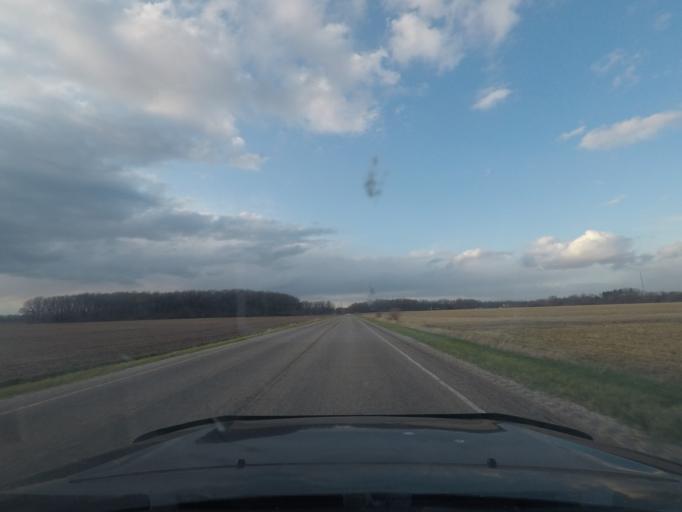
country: US
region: Indiana
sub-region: LaPorte County
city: LaPorte
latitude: 41.5409
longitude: -86.7405
